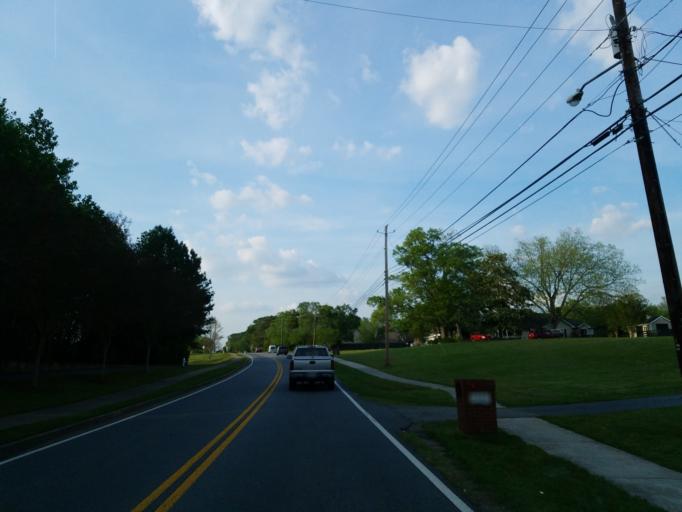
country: US
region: Georgia
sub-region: Fulton County
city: Roswell
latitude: 34.0701
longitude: -84.3606
